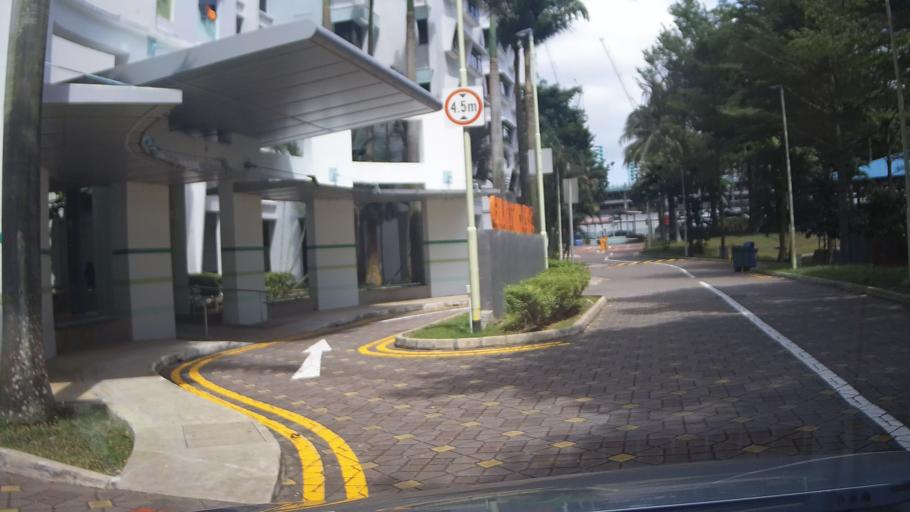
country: SG
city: Singapore
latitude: 1.3109
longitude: 103.7660
